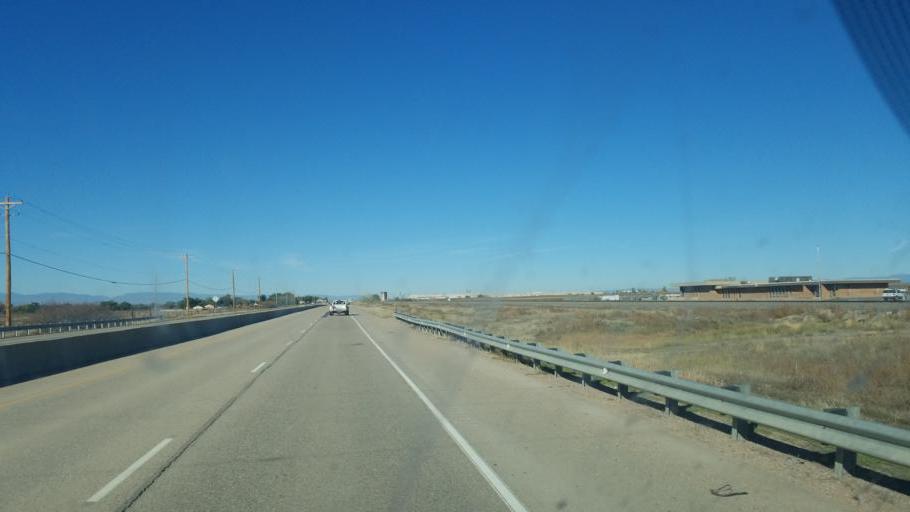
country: US
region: Colorado
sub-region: Pueblo County
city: Pueblo
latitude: 38.2737
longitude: -104.4463
